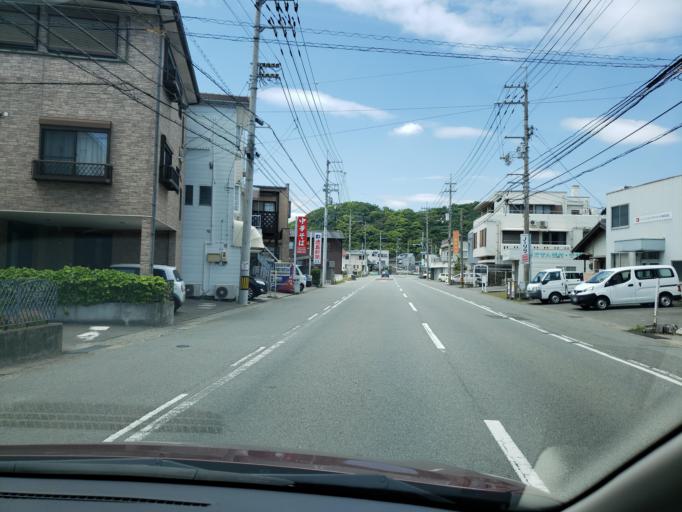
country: JP
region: Tokushima
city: Tokushima-shi
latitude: 34.0453
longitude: 134.5779
